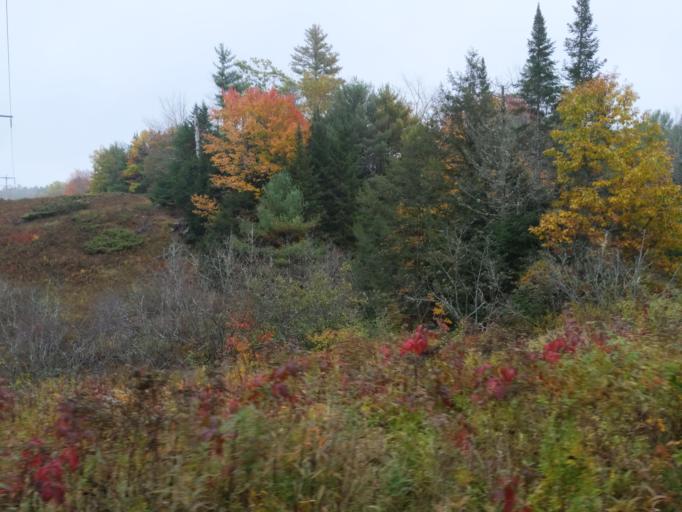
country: US
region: Maine
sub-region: Lincoln County
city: Wiscasset
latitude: 44.0685
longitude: -69.6228
